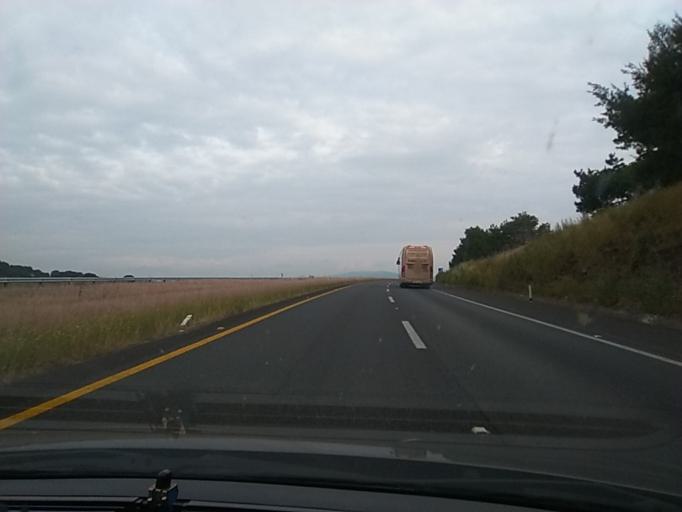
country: MX
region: Michoacan
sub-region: Puruandiro
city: San Lorenzo
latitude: 19.9607
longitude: -101.6725
